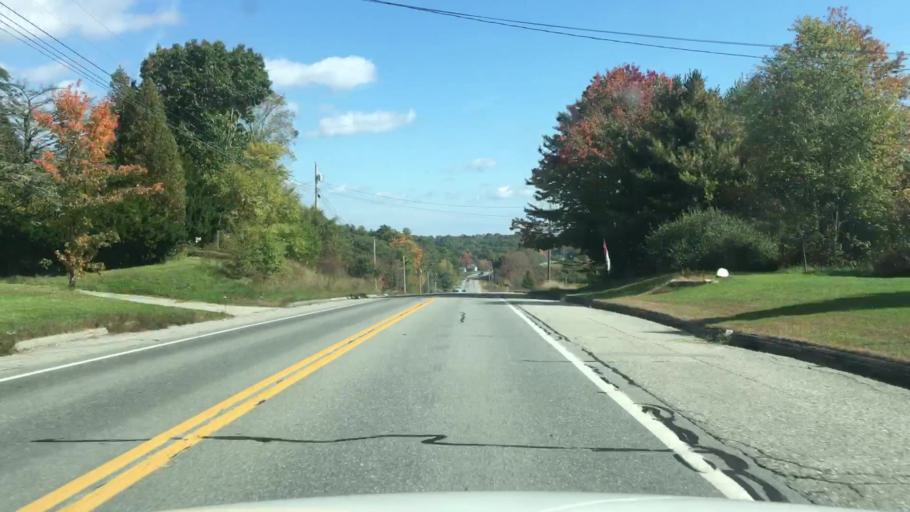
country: US
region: Maine
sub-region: Knox County
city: Warren
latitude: 44.1190
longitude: -69.2966
